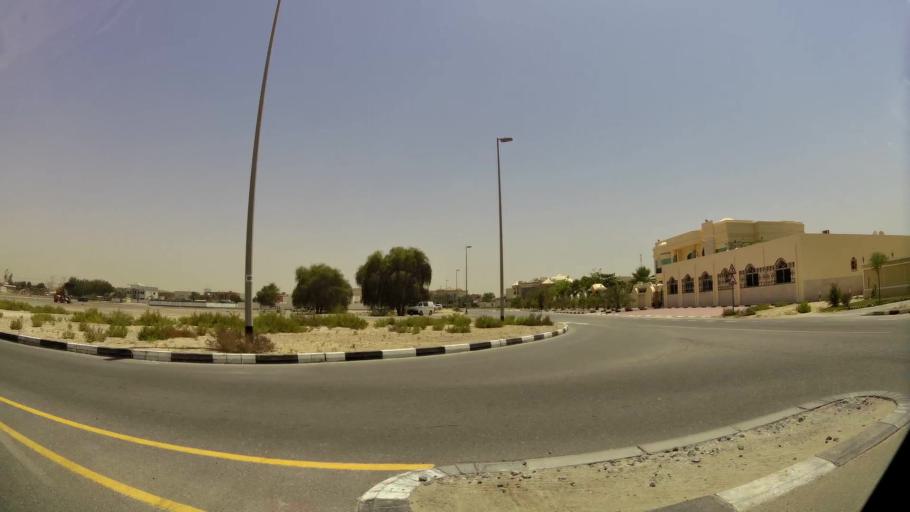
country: AE
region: Dubai
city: Dubai
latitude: 25.0884
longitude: 55.2049
